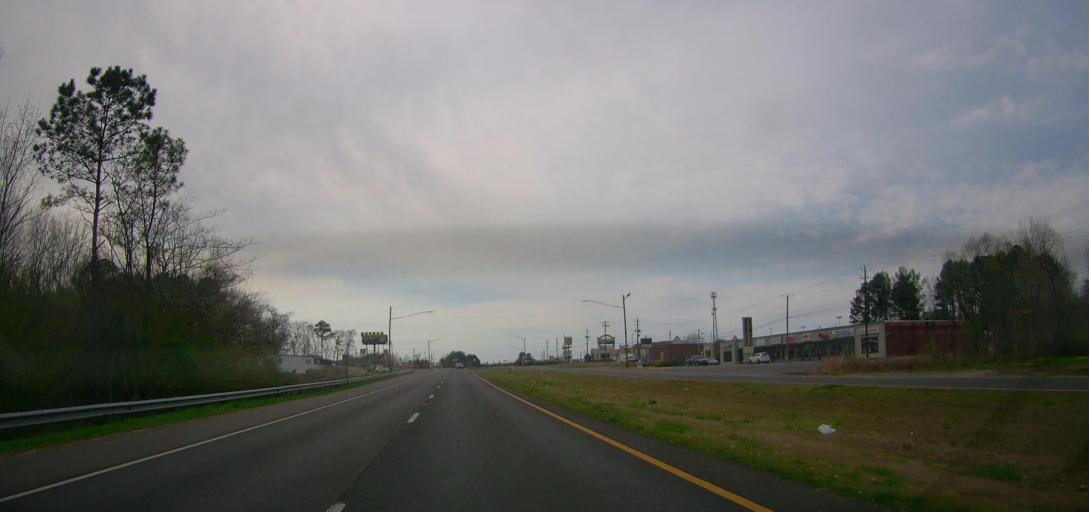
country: US
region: Alabama
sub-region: Walker County
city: Jasper
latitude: 33.8471
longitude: -87.2640
